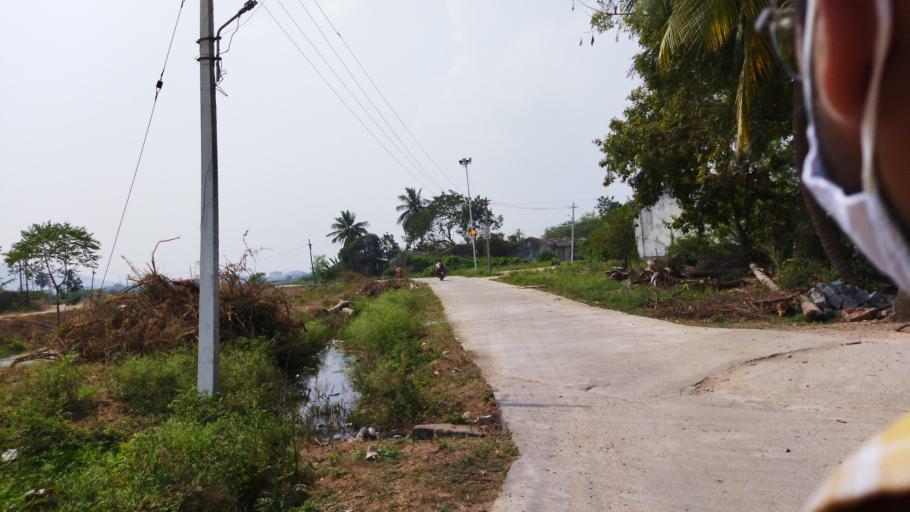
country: IN
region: Telangana
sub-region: Nalgonda
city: Nalgonda
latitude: 17.0846
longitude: 79.2739
